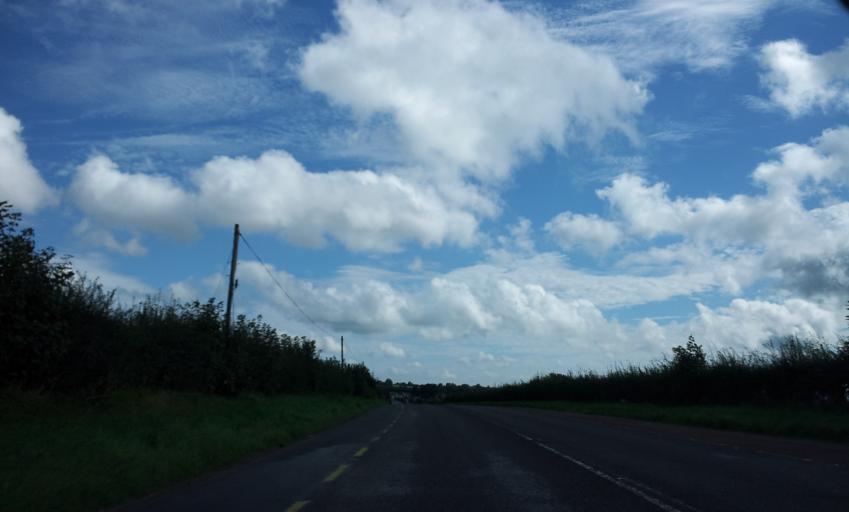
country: IE
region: Leinster
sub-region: Laois
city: Rathdowney
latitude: 52.9486
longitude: -7.5682
